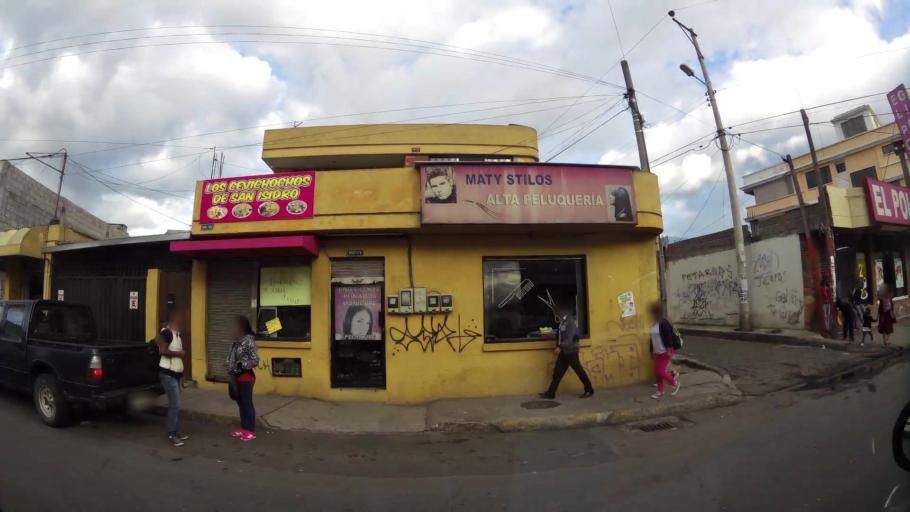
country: EC
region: Pichincha
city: Quito
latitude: -0.1474
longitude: -78.4655
